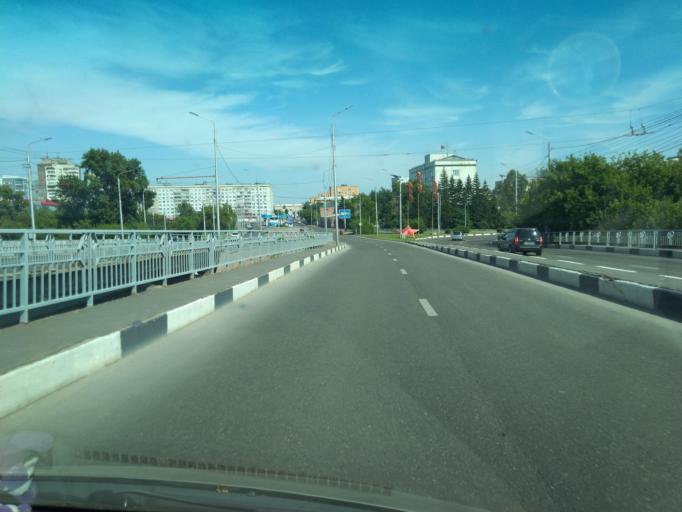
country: RU
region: Krasnoyarskiy
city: Krasnoyarsk
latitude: 56.0124
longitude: 92.8348
